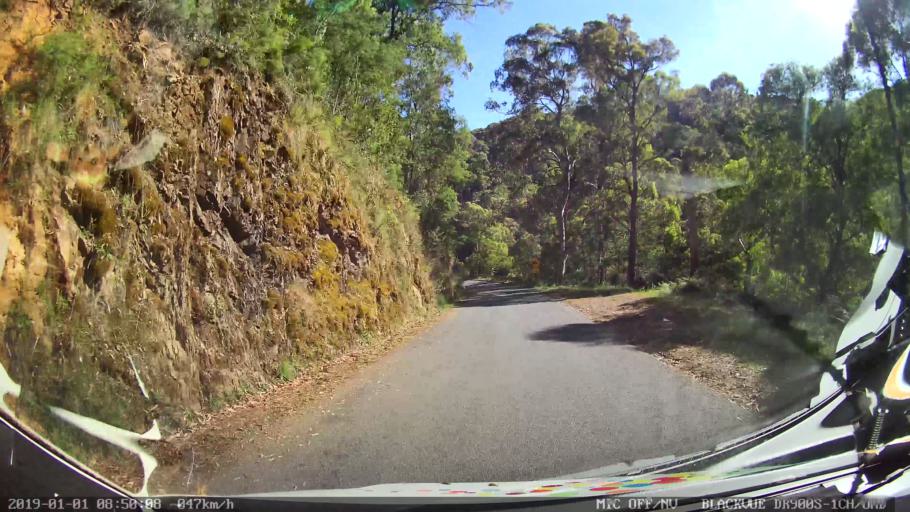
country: AU
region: New South Wales
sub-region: Snowy River
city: Jindabyne
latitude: -36.2780
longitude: 148.2023
